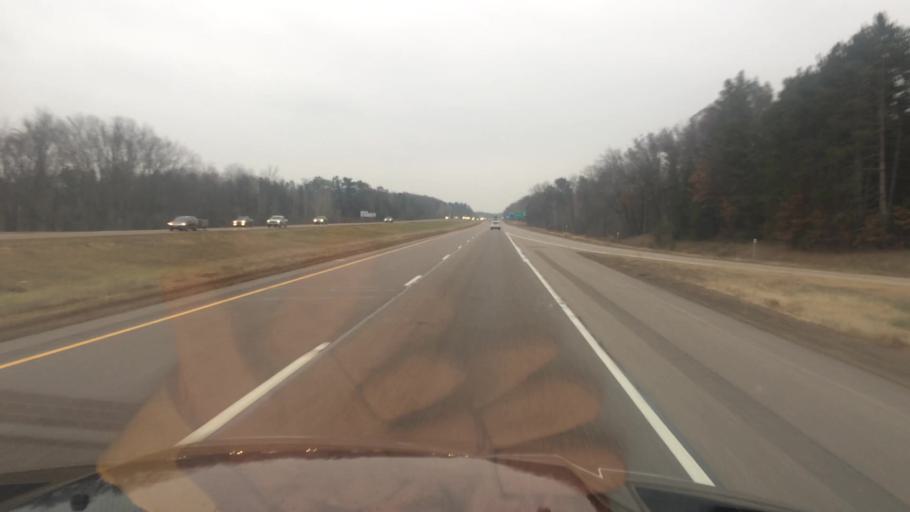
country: US
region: Wisconsin
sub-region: Portage County
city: Stevens Point
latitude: 44.5686
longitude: -89.5974
